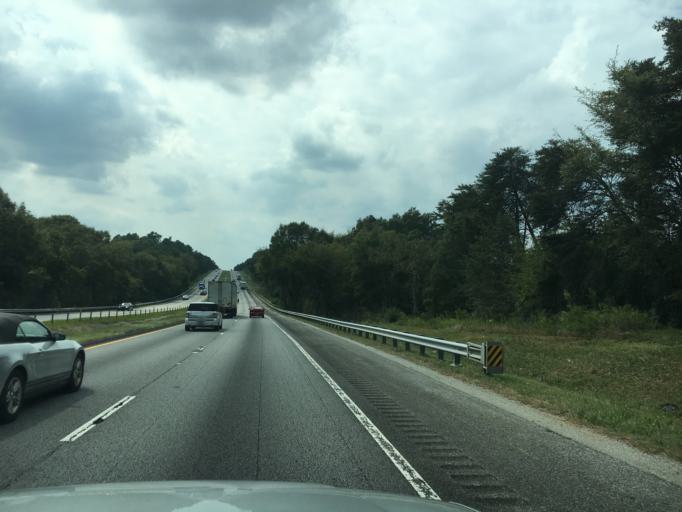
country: US
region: South Carolina
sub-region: Anderson County
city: Centerville
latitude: 34.5629
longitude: -82.7579
